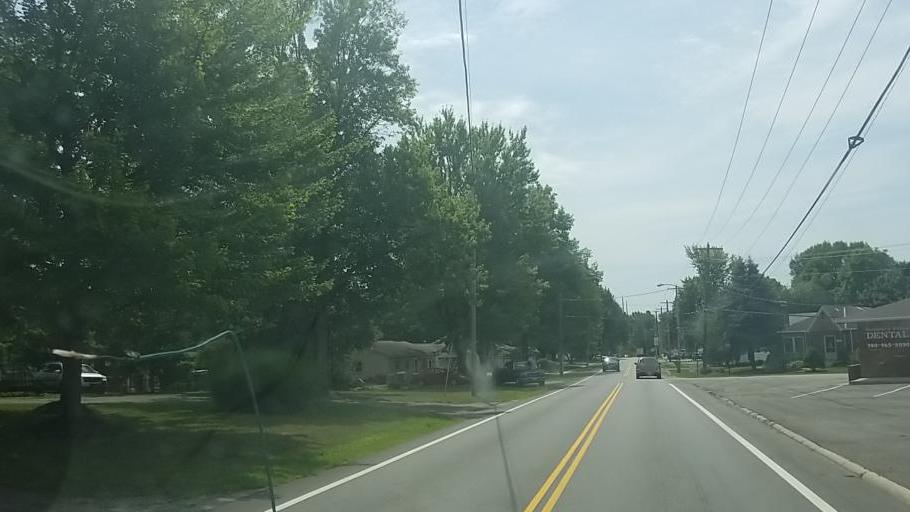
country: US
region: Ohio
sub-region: Delaware County
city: Sunbury
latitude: 40.2391
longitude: -82.8544
